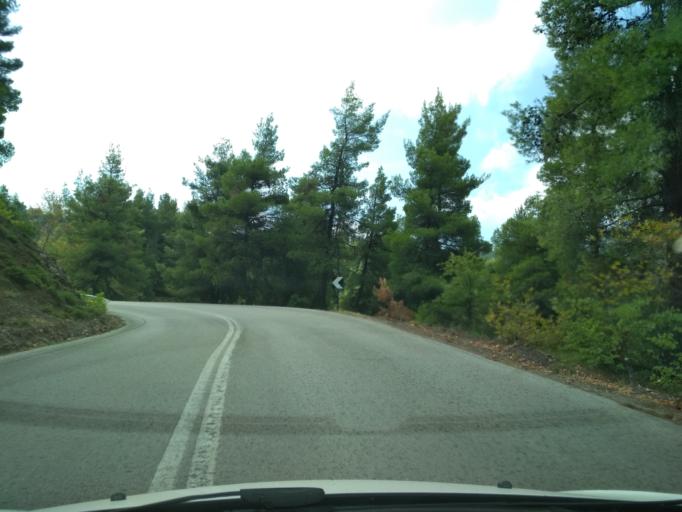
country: GR
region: Central Greece
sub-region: Nomos Evvoias
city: Politika
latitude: 38.6696
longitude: 23.5578
